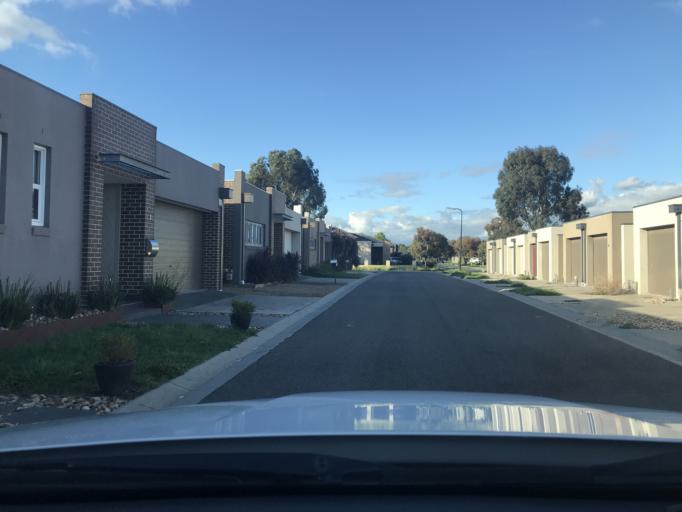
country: AU
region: Victoria
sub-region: Hume
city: Craigieburn
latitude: -37.5788
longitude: 144.9080
